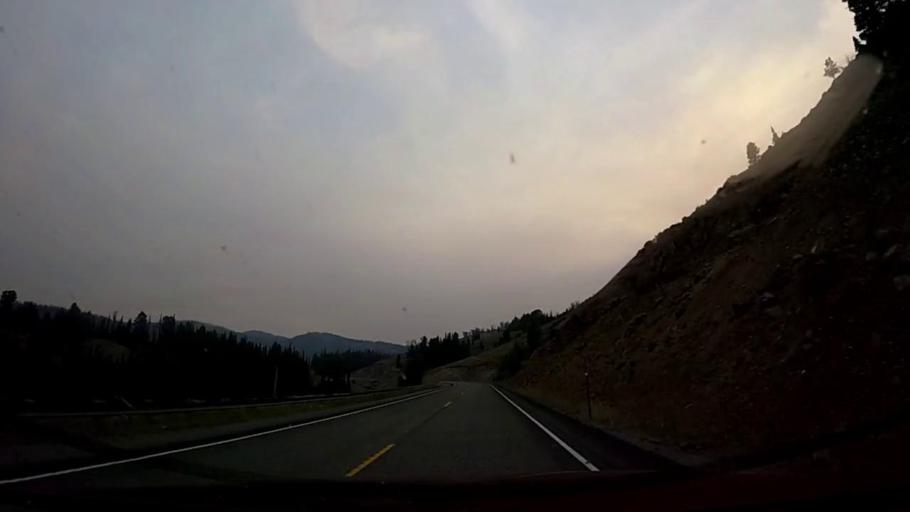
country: US
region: Idaho
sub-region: Blaine County
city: Ketchum
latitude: 43.8778
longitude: -114.7029
